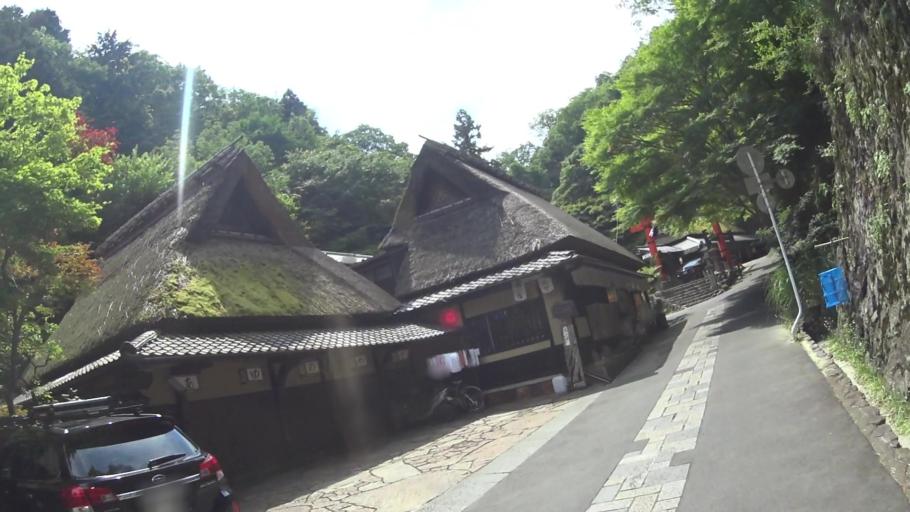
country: JP
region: Kyoto
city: Muko
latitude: 35.0282
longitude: 135.6629
